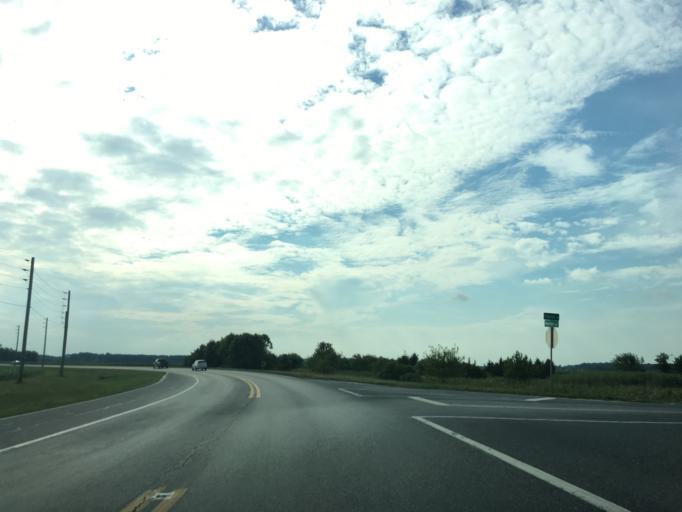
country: US
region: Delaware
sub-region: Sussex County
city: Bridgeville
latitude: 38.7631
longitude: -75.6104
